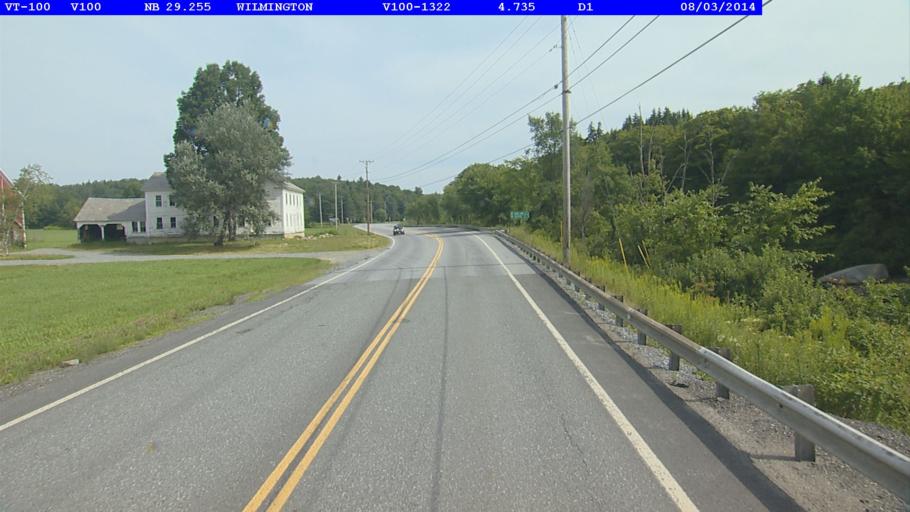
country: US
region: Vermont
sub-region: Windham County
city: Dover
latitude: 42.8946
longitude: -72.8559
